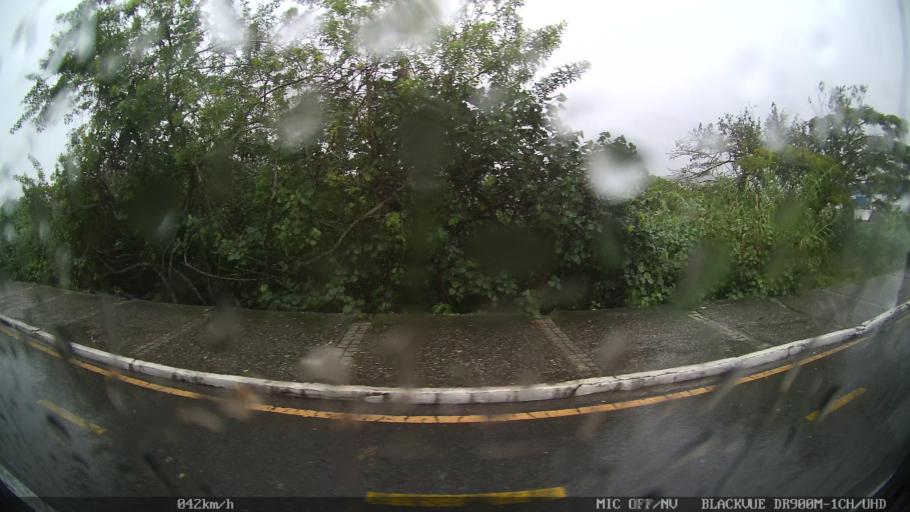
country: BR
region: Santa Catarina
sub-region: Balneario Camboriu
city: Balneario Camboriu
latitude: -27.0111
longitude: -48.6321
